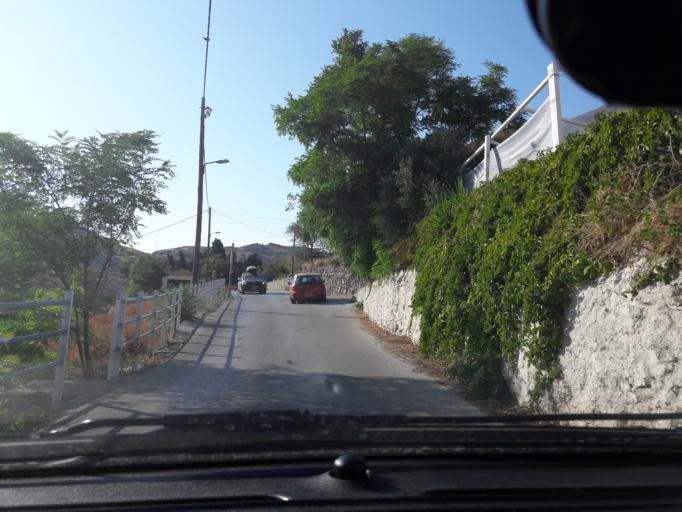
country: GR
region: North Aegean
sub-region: Nomos Lesvou
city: Myrina
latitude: 39.8566
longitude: 25.0851
